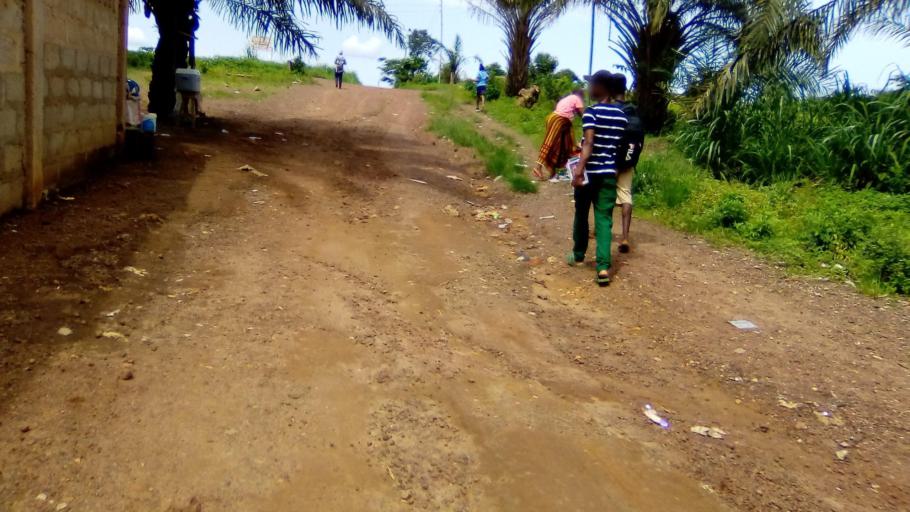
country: SL
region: Southern Province
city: Bo
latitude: 7.9344
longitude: -11.7215
